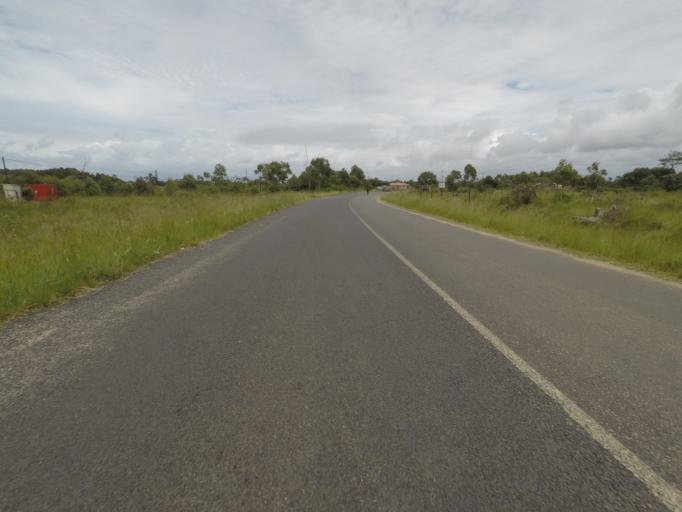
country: ZA
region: KwaZulu-Natal
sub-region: uThungulu District Municipality
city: eSikhawini
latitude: -28.9097
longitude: 31.8788
